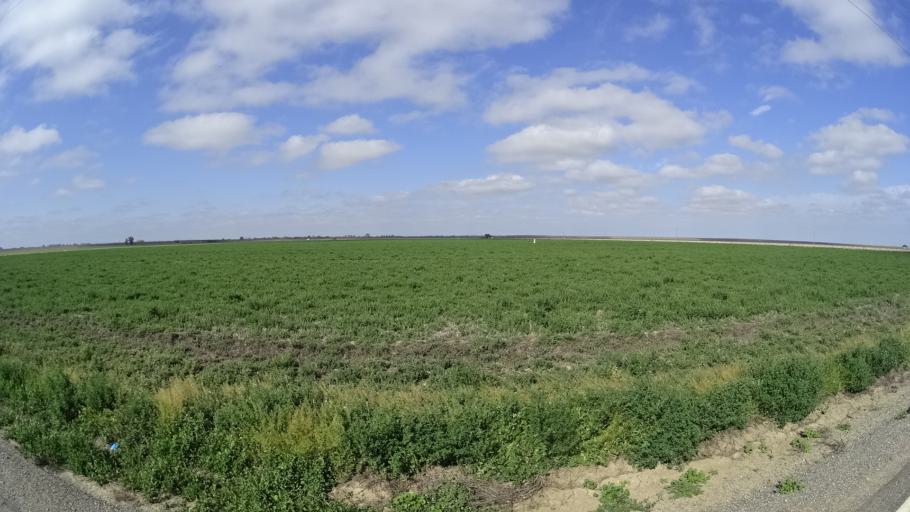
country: US
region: California
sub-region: Butte County
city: Biggs
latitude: 39.4260
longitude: -121.9296
